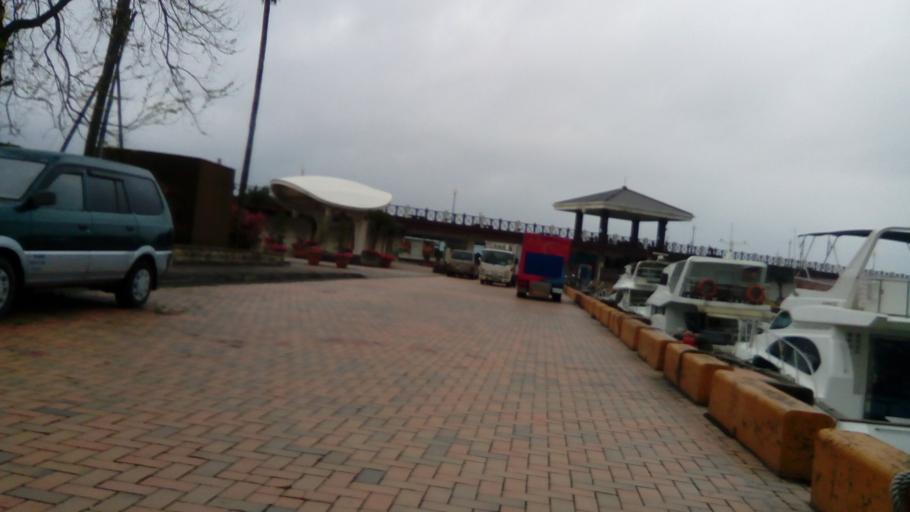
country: TW
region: Taipei
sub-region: Taipei
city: Banqiao
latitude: 25.1825
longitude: 121.4136
